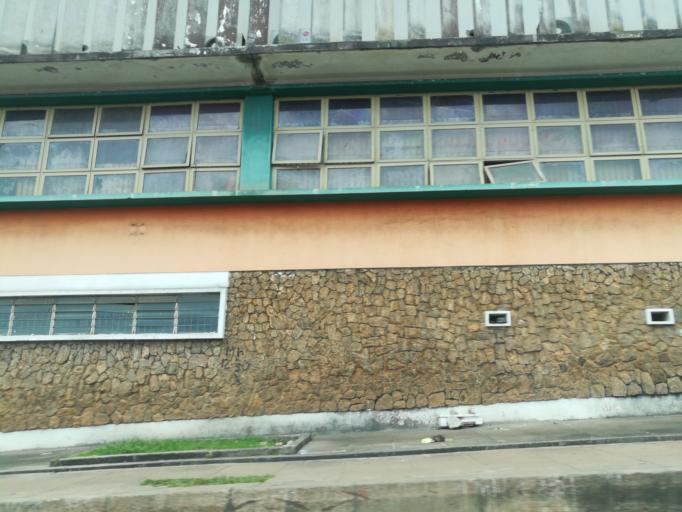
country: NG
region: Oyo
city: Ibadan
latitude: 7.3864
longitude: 3.8813
